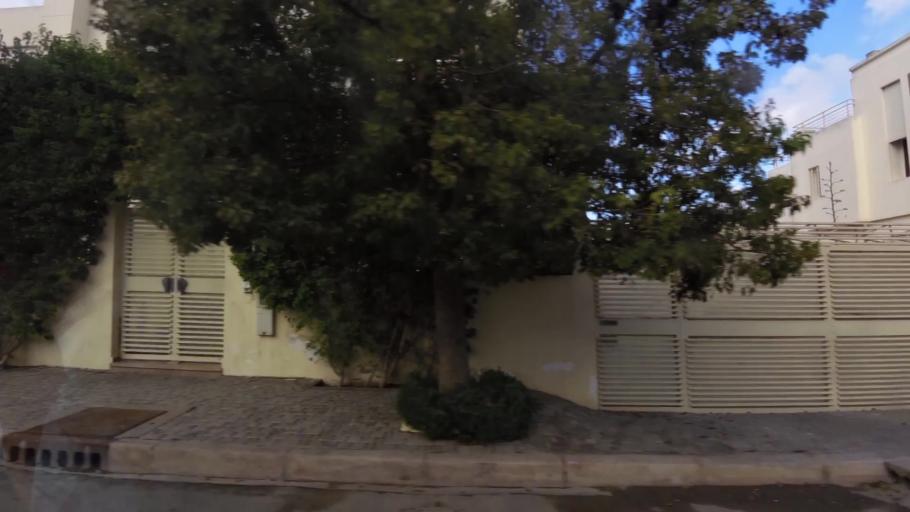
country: MA
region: Grand Casablanca
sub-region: Casablanca
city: Casablanca
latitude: 33.5762
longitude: -7.6968
